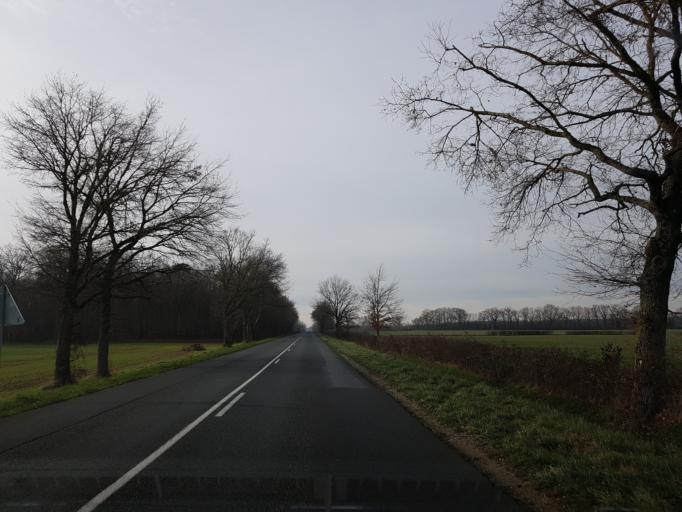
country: FR
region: Auvergne
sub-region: Departement de l'Allier
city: Lusigny
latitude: 46.5786
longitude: 3.4287
